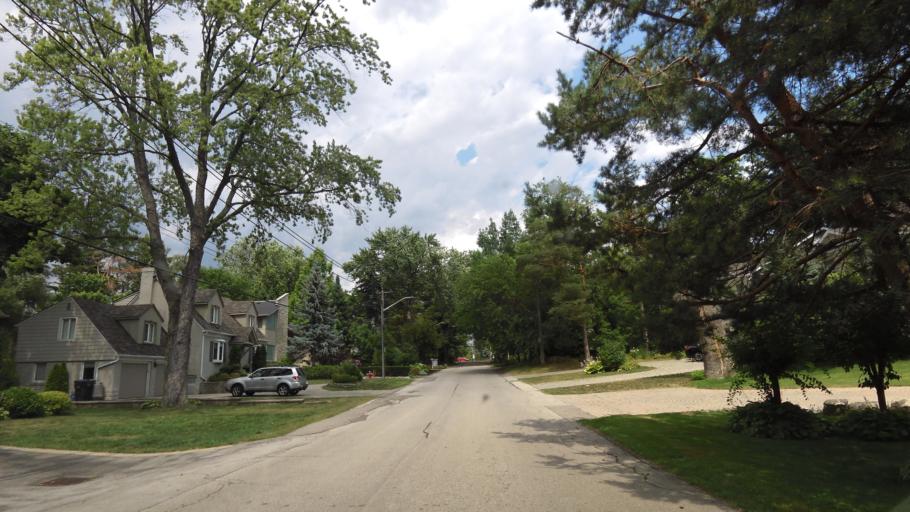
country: CA
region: Ontario
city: Mississauga
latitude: 43.5632
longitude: -79.5961
